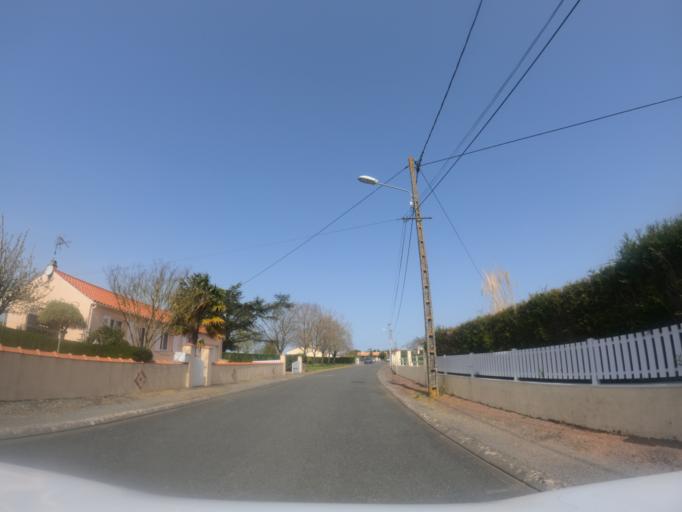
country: FR
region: Pays de la Loire
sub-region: Departement de la Vendee
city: Vix
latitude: 46.3942
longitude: -0.8139
